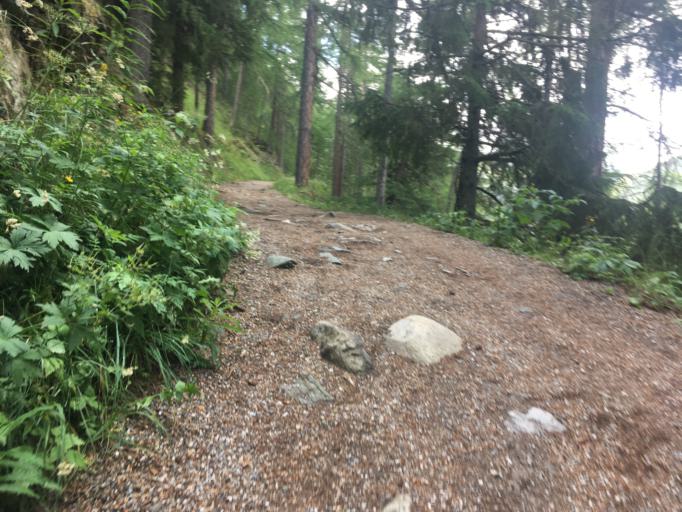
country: CH
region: Valais
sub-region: Visp District
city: Zermatt
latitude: 46.0125
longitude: 7.7508
